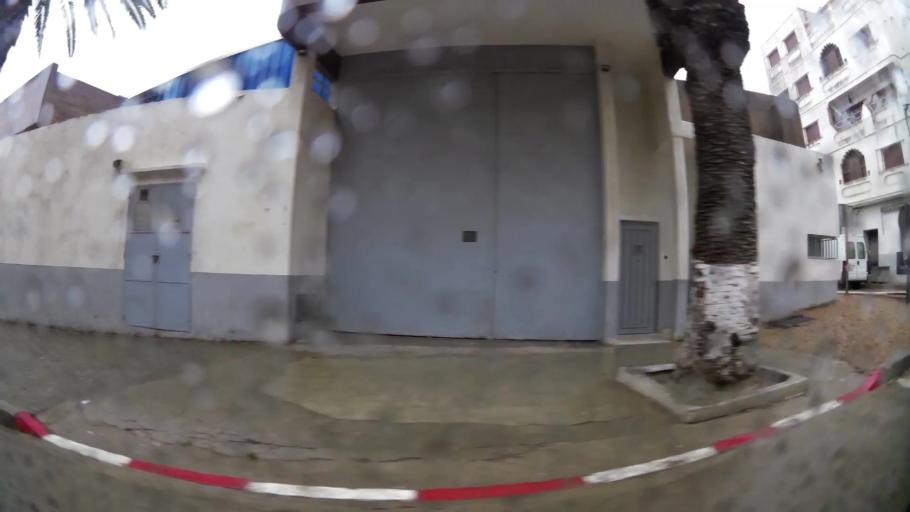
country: MA
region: Taza-Al Hoceima-Taounate
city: Al Hoceima
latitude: 35.2445
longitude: -3.9304
